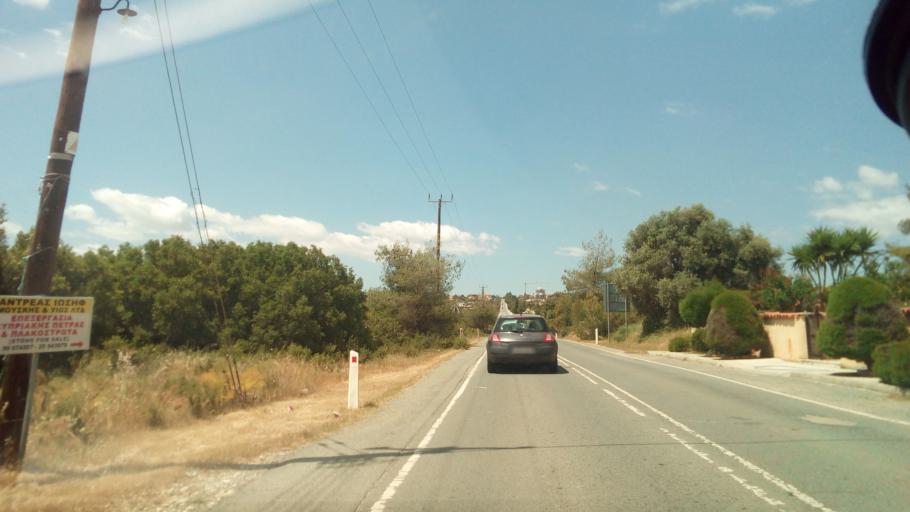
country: CY
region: Limassol
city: Sotira
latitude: 34.7515
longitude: 32.8663
